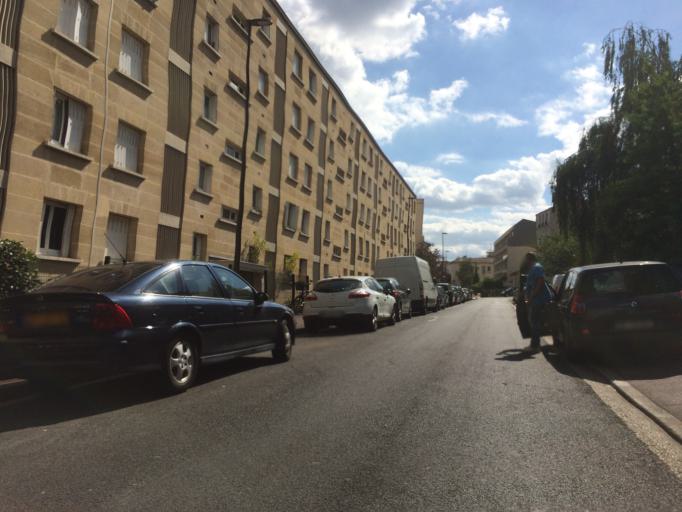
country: FR
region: Ile-de-France
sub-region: Departement des Hauts-de-Seine
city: Suresnes
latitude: 48.8772
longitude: 2.2288
